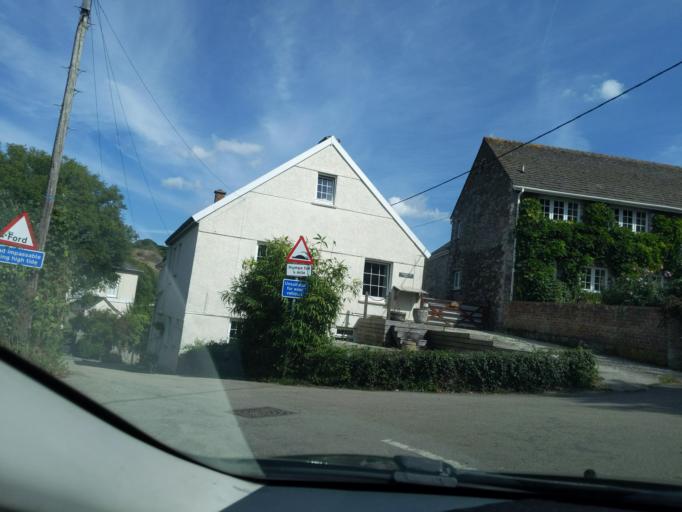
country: GB
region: England
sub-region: Cornwall
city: Torpoint
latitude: 50.3605
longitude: -4.2374
